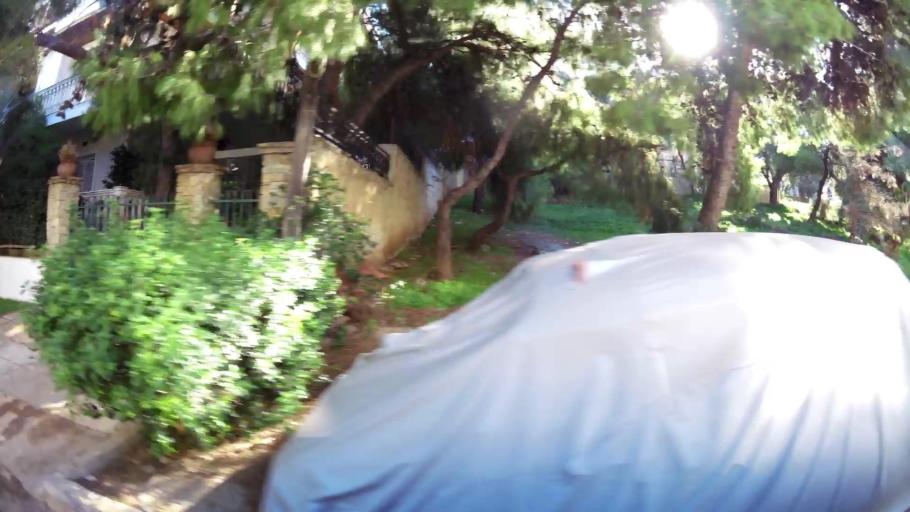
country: GR
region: Attica
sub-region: Nomarchia Anatolikis Attikis
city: Voula
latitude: 37.8558
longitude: 23.7715
